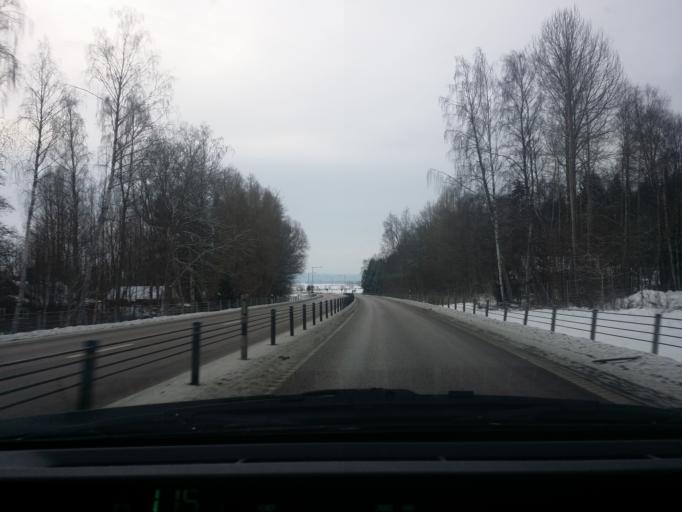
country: SE
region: Vaestra Goetaland
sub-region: Mariestads Kommun
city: Mariestad
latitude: 58.5983
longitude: 13.7981
